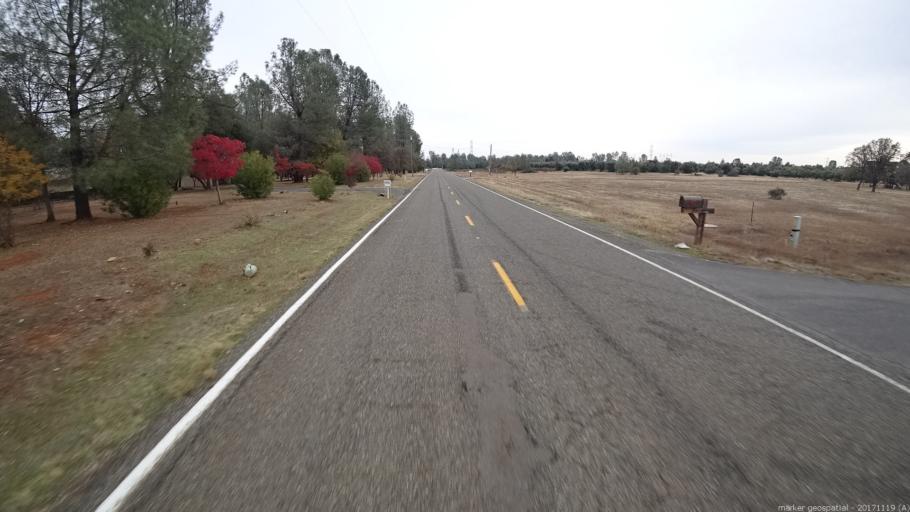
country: US
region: California
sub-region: Shasta County
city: Redding
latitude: 40.4882
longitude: -122.4330
